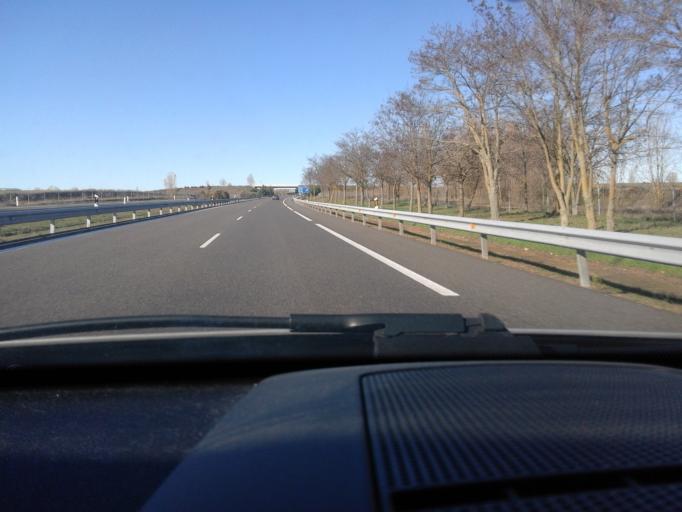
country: ES
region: Castille and Leon
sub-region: Provincia de Leon
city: Sahagun
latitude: 42.3765
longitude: -5.0051
